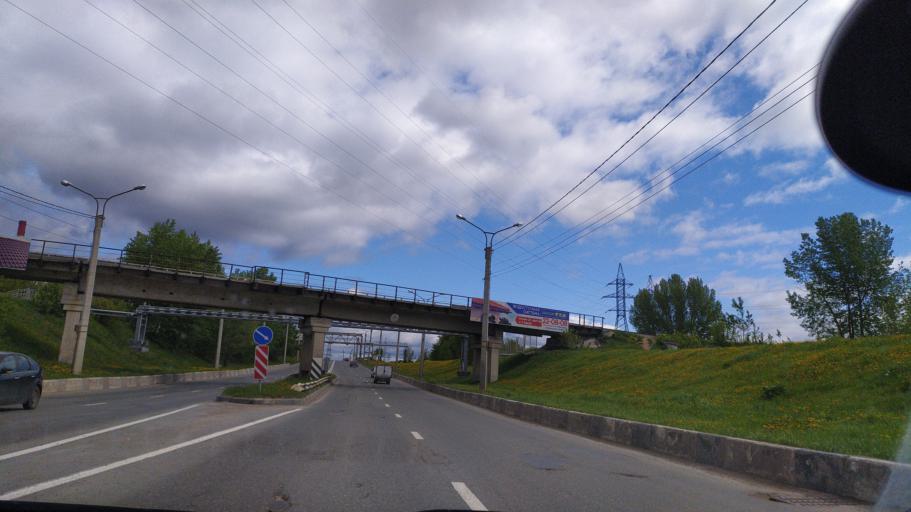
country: RU
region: Chuvashia
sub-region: Cheboksarskiy Rayon
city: Cheboksary
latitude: 56.1126
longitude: 47.2967
